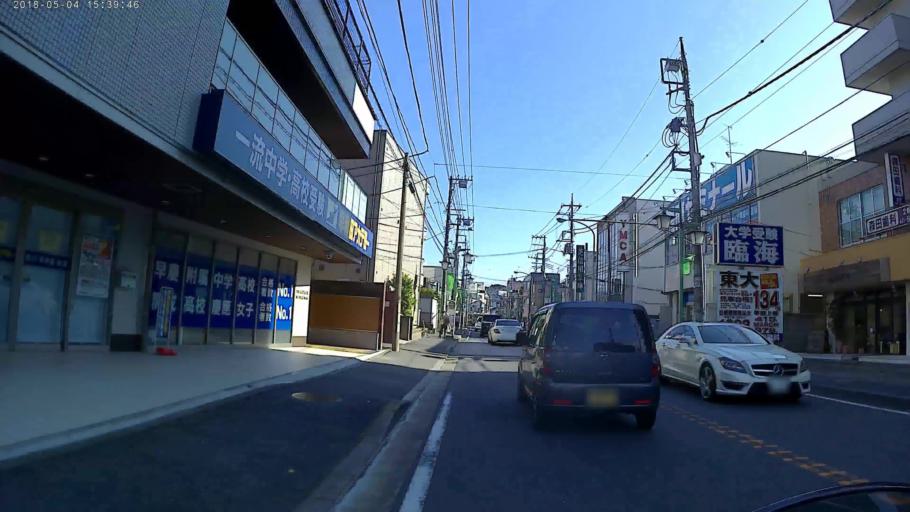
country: JP
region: Kanagawa
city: Yokohama
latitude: 35.5122
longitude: 139.6319
